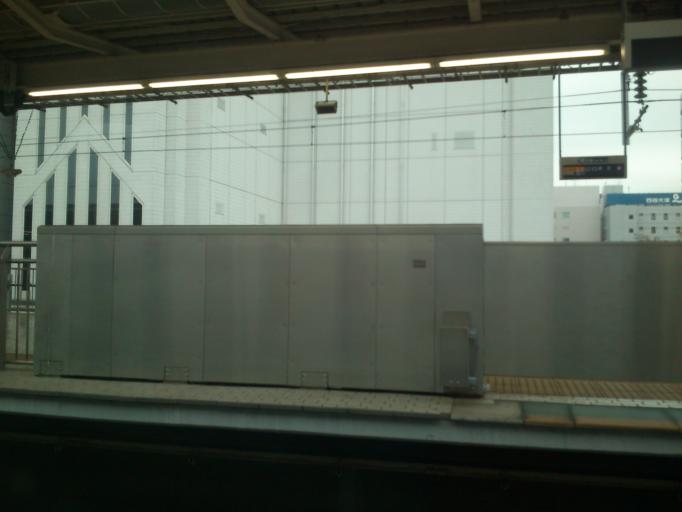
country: JP
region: Kanagawa
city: Yokohama
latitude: 35.5087
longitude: 139.6190
